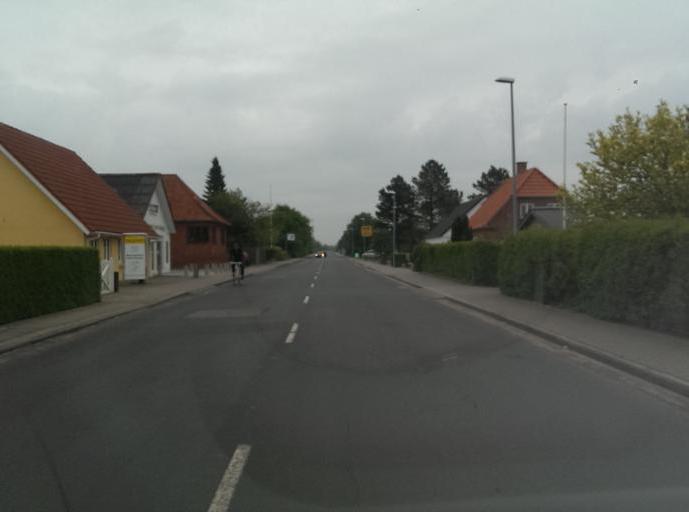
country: DK
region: South Denmark
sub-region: Esbjerg Kommune
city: Esbjerg
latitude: 55.5255
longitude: 8.4629
